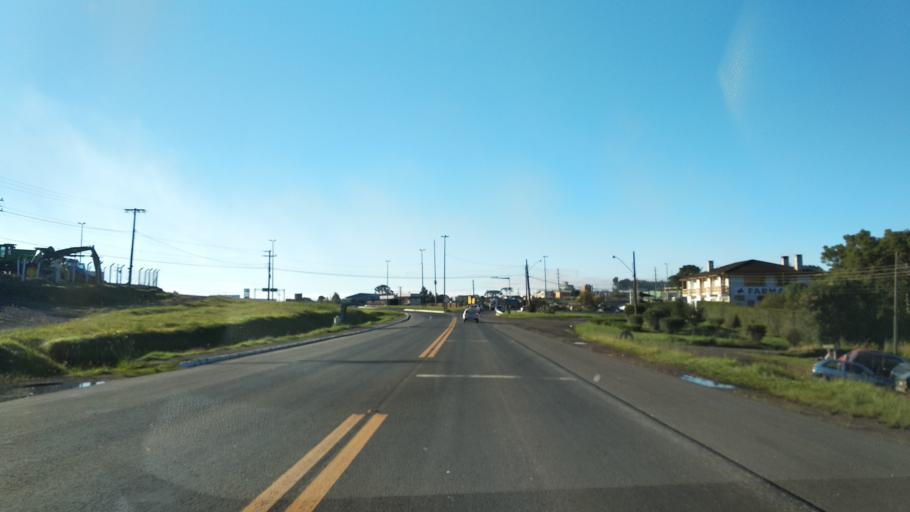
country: BR
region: Santa Catarina
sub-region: Lages
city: Lages
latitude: -27.7991
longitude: -50.3649
